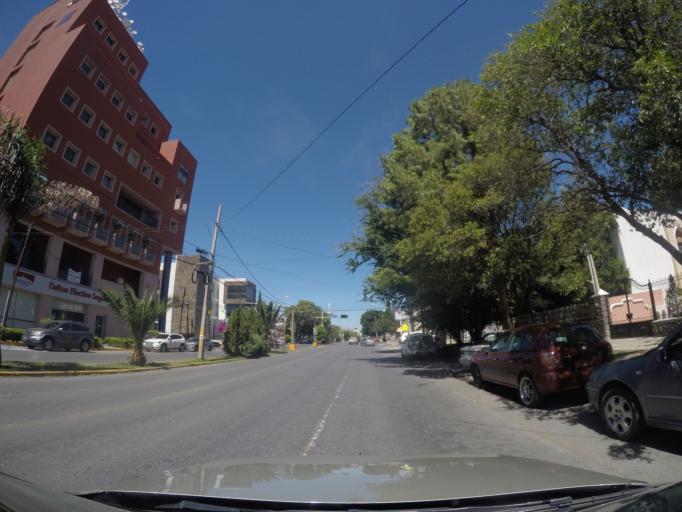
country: MX
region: San Luis Potosi
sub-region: San Luis Potosi
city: San Luis Potosi
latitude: 22.1489
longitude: -101.0078
